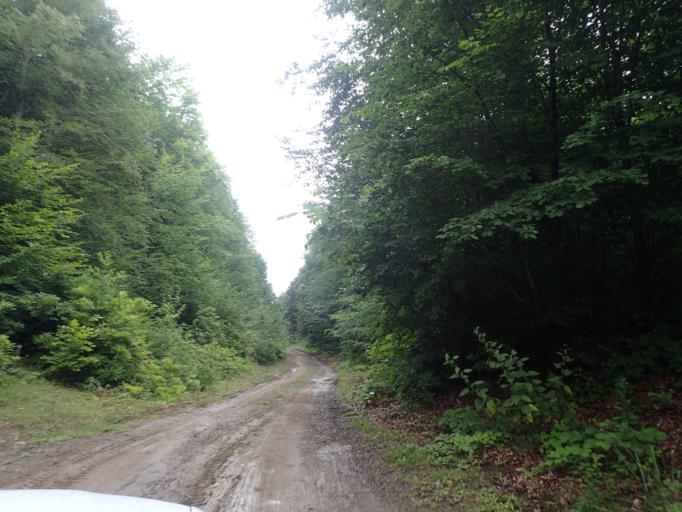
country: TR
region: Ordu
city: Akkus
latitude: 40.8117
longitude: 37.0822
